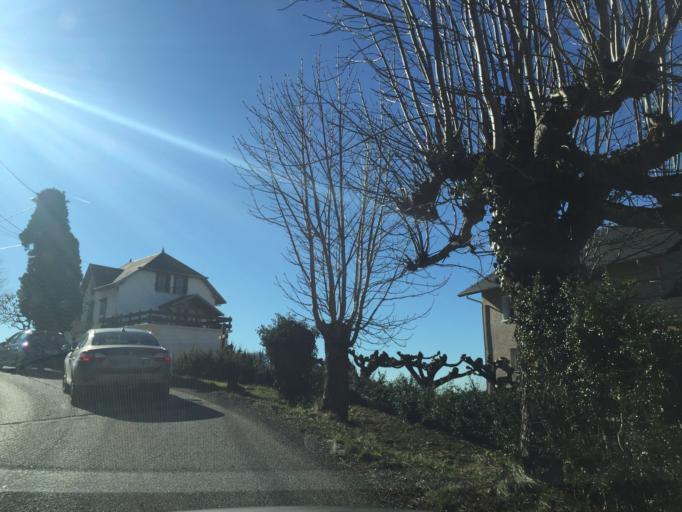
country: FR
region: Rhone-Alpes
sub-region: Departement de la Savoie
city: Mouxy
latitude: 45.7009
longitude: 5.9672
